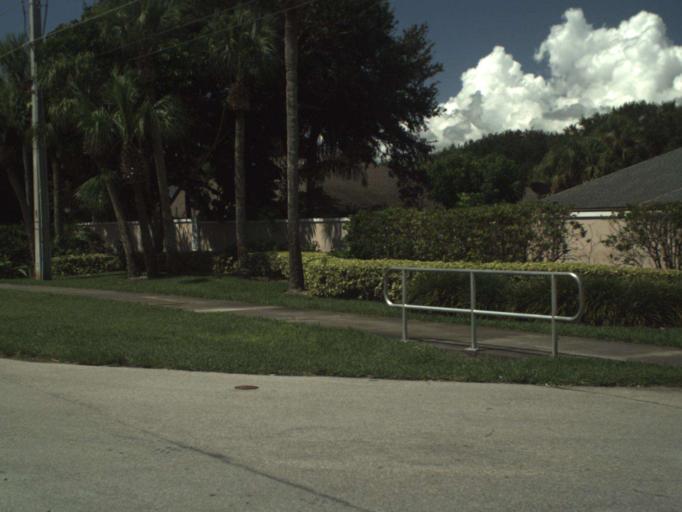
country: US
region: Florida
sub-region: Indian River County
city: South Beach
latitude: 27.6230
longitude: -80.3524
